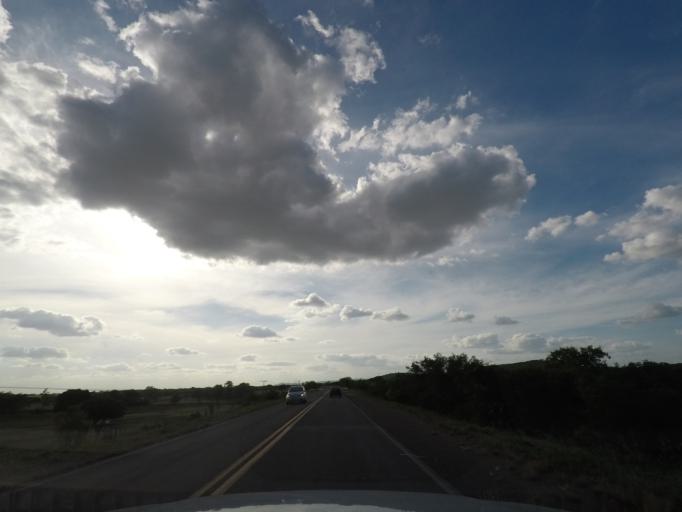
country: BR
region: Bahia
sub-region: Ipira
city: Ipira
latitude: -12.1867
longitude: -39.4915
